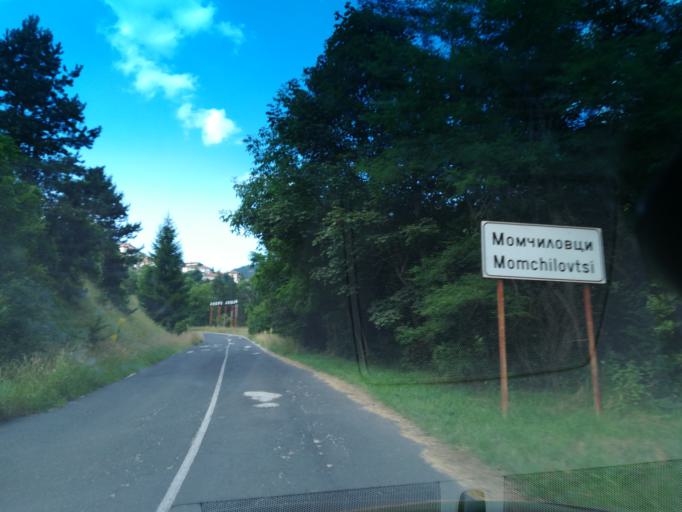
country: BG
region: Smolyan
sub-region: Obshtina Smolyan
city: Smolyan
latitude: 41.6516
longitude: 24.7718
